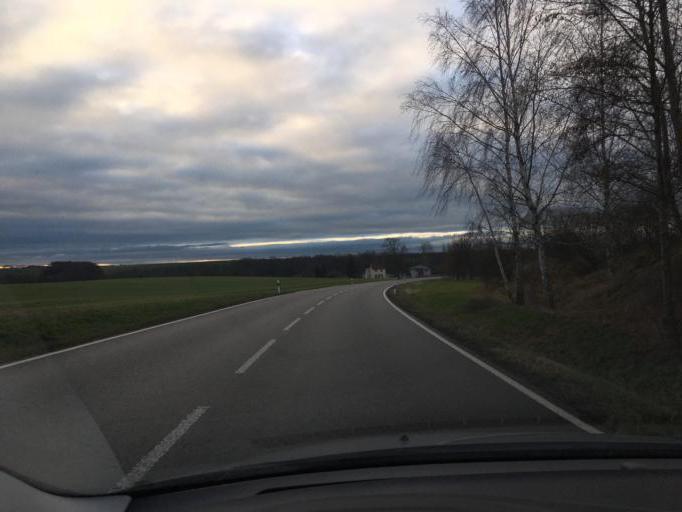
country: DE
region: Saxony
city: Frohburg
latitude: 51.0146
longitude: 12.5621
